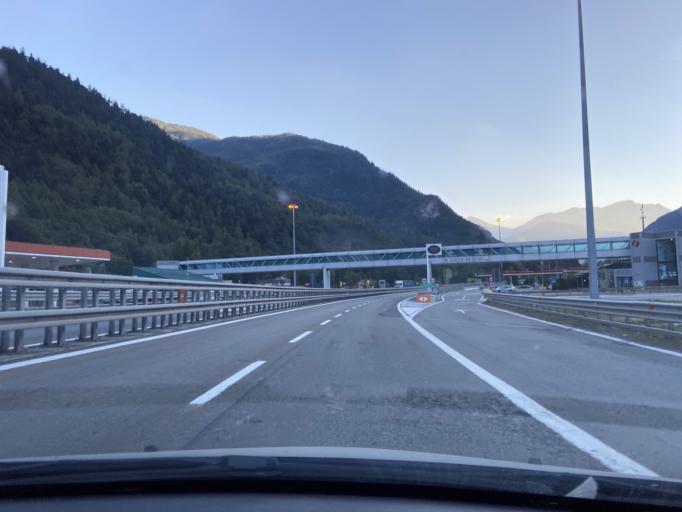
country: IT
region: Piedmont
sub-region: Provincia di Torino
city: Salbertrand
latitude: 45.0725
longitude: 6.8932
